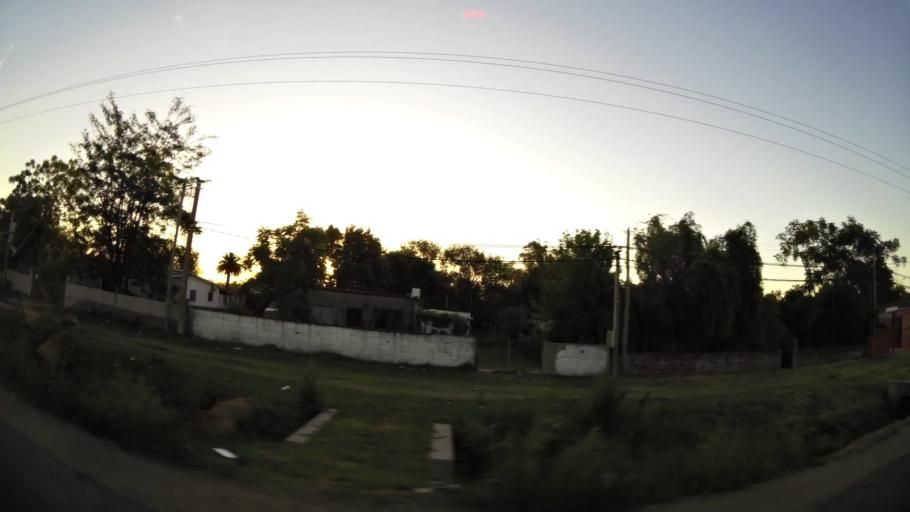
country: UY
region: Montevideo
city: Montevideo
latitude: -34.8250
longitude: -56.1687
